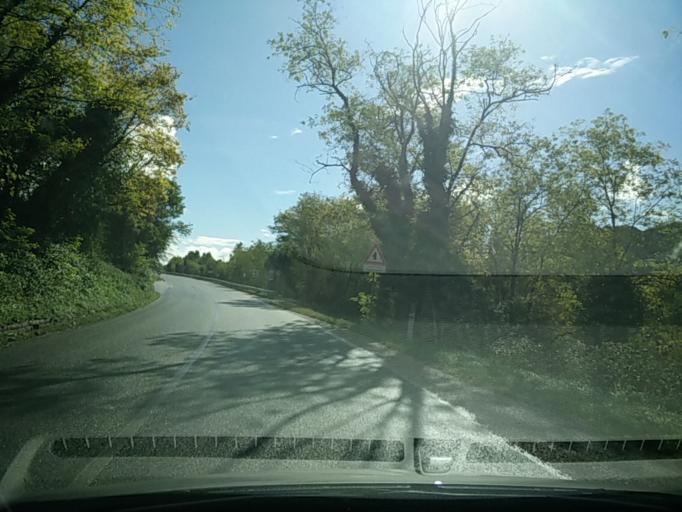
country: IT
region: Veneto
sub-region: Provincia di Treviso
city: Segusino
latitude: 45.8978
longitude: 11.9527
